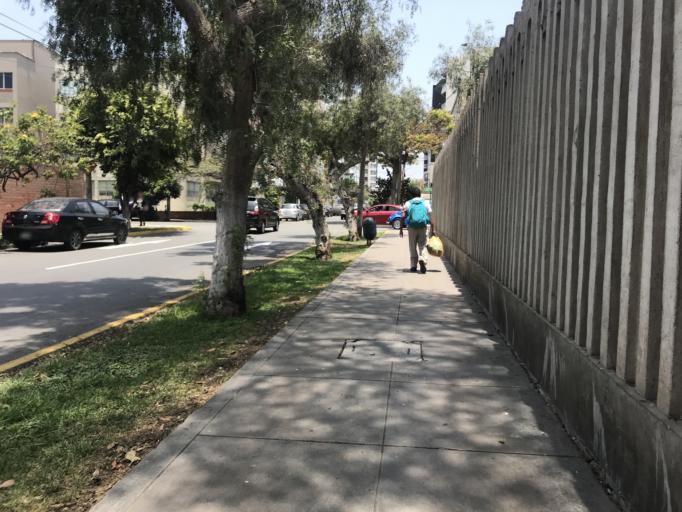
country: PE
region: Lima
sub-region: Lima
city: San Isidro
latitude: -12.1096
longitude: -77.0328
